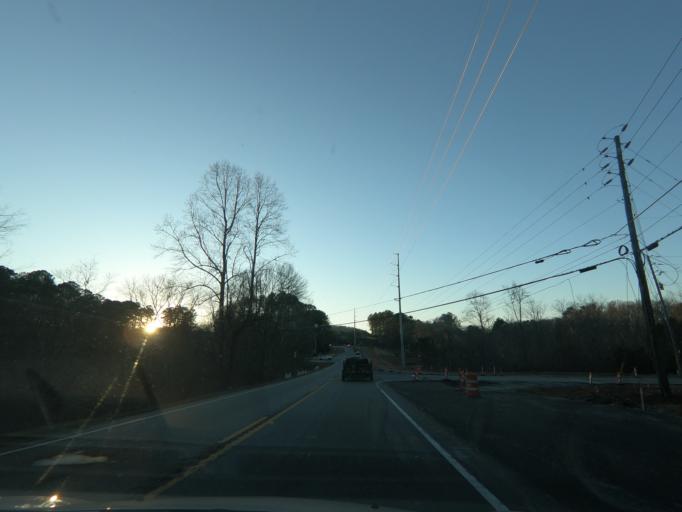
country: US
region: Georgia
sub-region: Forsyth County
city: Cumming
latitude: 34.3060
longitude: -84.2119
